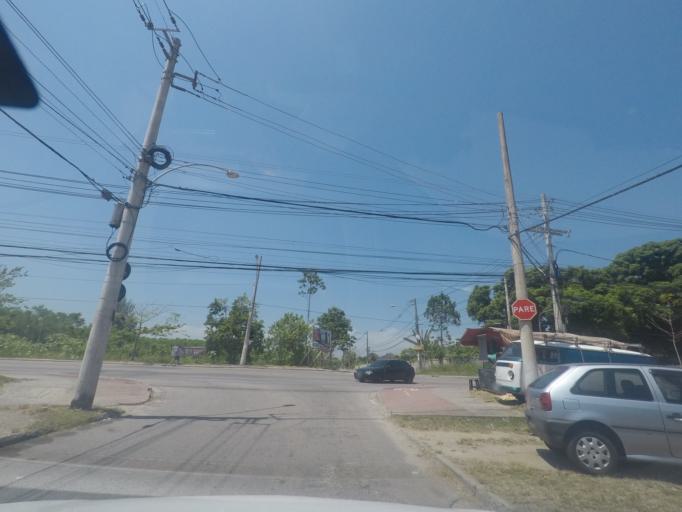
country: BR
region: Rio de Janeiro
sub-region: Nilopolis
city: Nilopolis
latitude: -22.9854
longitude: -43.4597
